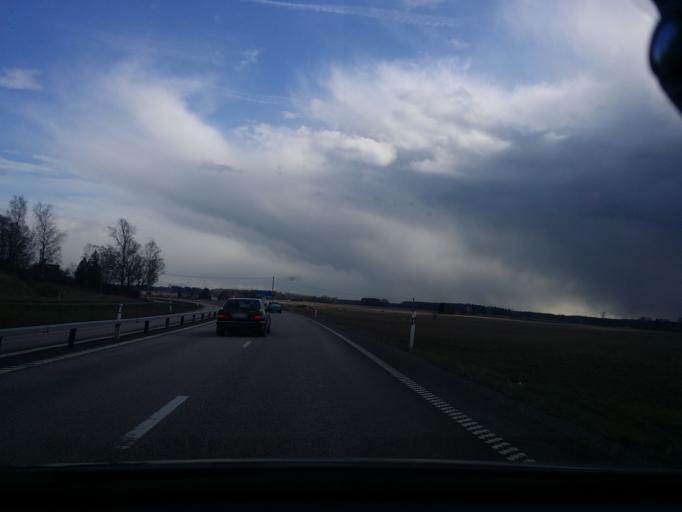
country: SE
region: Vaestmanland
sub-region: Vasteras
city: Hokasen
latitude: 59.7303
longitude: 16.5649
